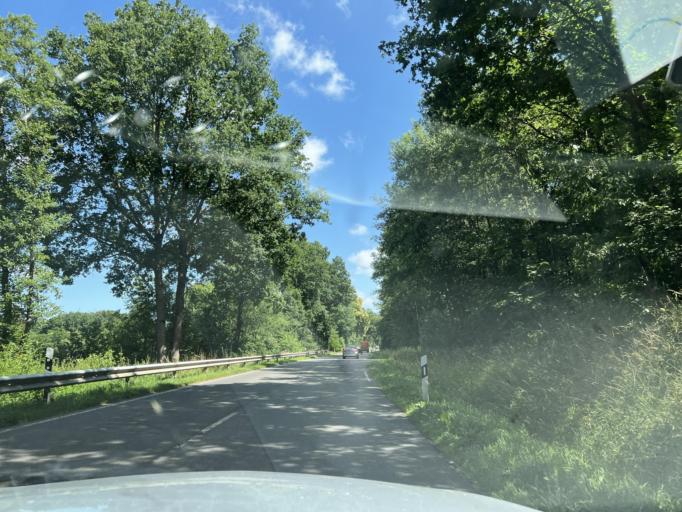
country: DE
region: North Rhine-Westphalia
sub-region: Regierungsbezirk Arnsberg
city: Wenden
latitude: 50.9754
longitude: 7.8357
